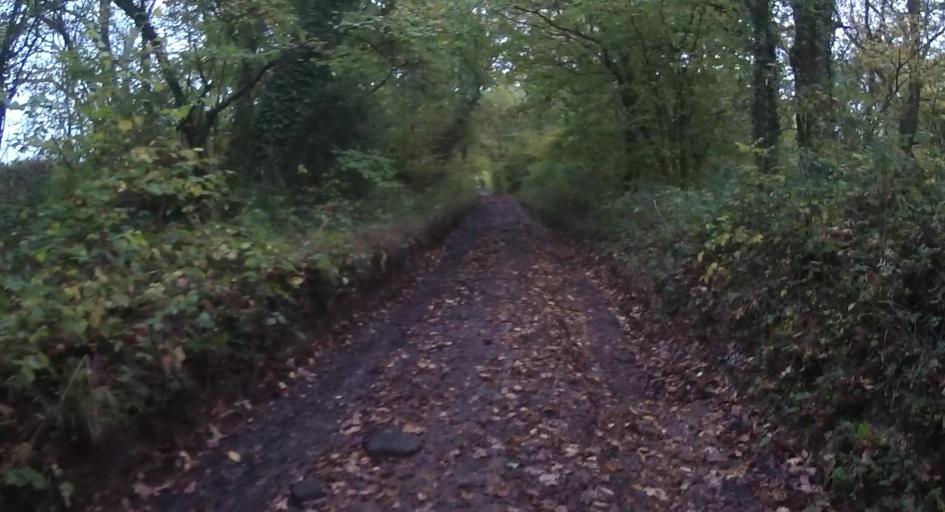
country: GB
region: England
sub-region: Surrey
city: Farnham
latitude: 51.2268
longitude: -0.8105
